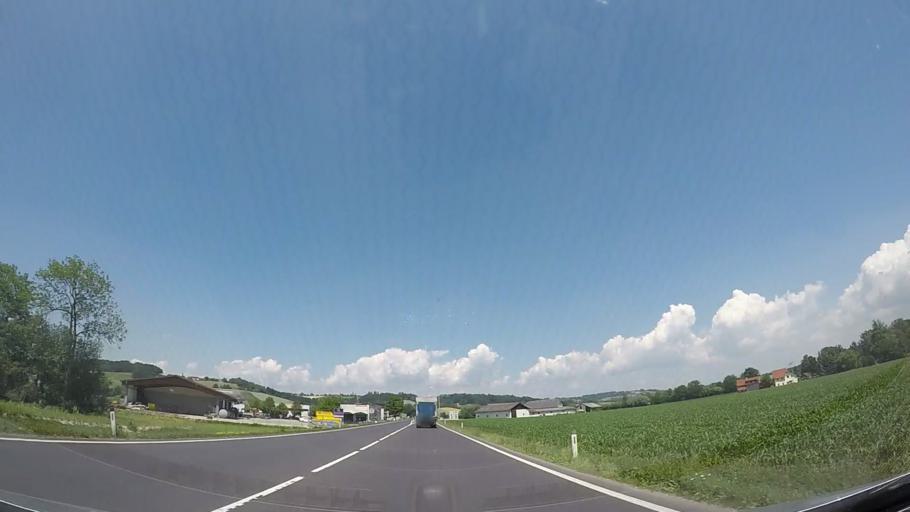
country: AT
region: Upper Austria
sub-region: Politischer Bezirk Grieskirchen
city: Bad Schallerbach
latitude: 48.2021
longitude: 13.9274
